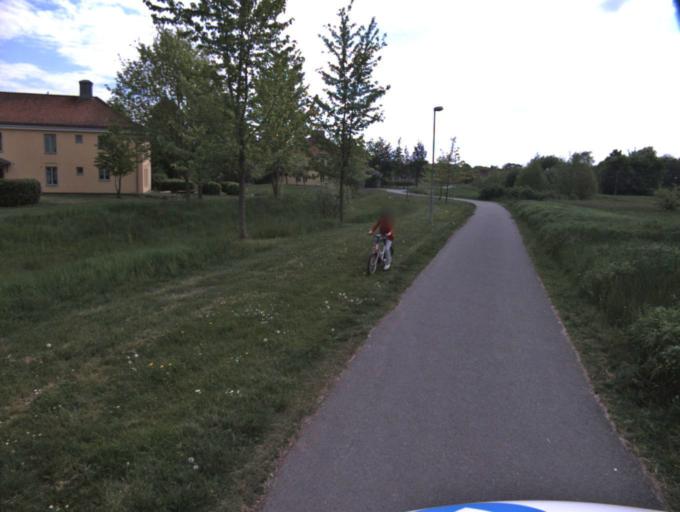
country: SE
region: Skane
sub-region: Kristianstads Kommun
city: Kristianstad
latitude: 56.0519
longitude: 14.1489
